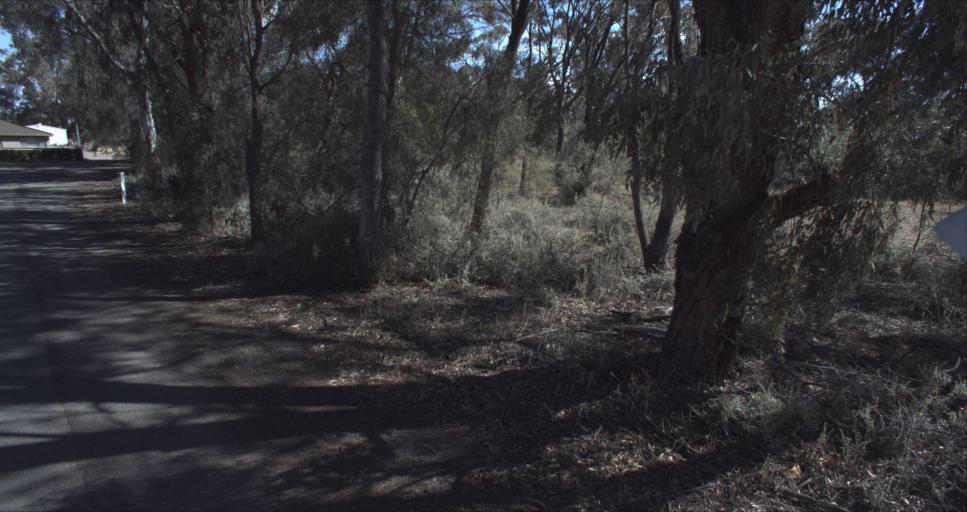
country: AU
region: New South Wales
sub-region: Leeton
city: Leeton
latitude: -34.5596
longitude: 146.3884
